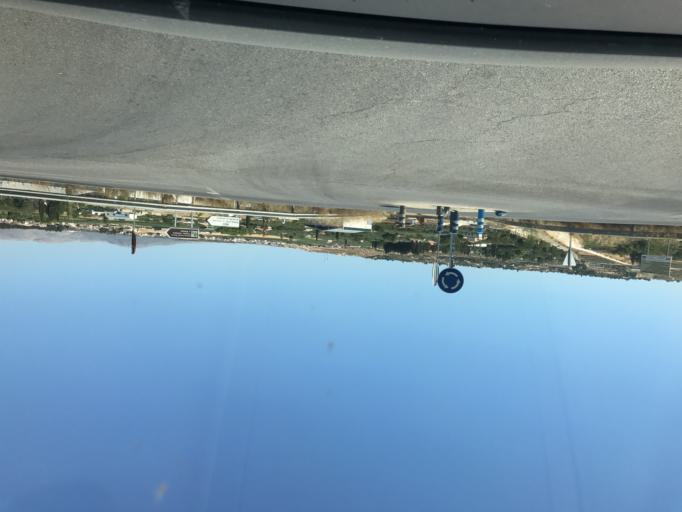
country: ES
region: Andalusia
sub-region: Provincia de Granada
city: Moraleda de Zafayona
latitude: 37.1814
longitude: -3.9486
